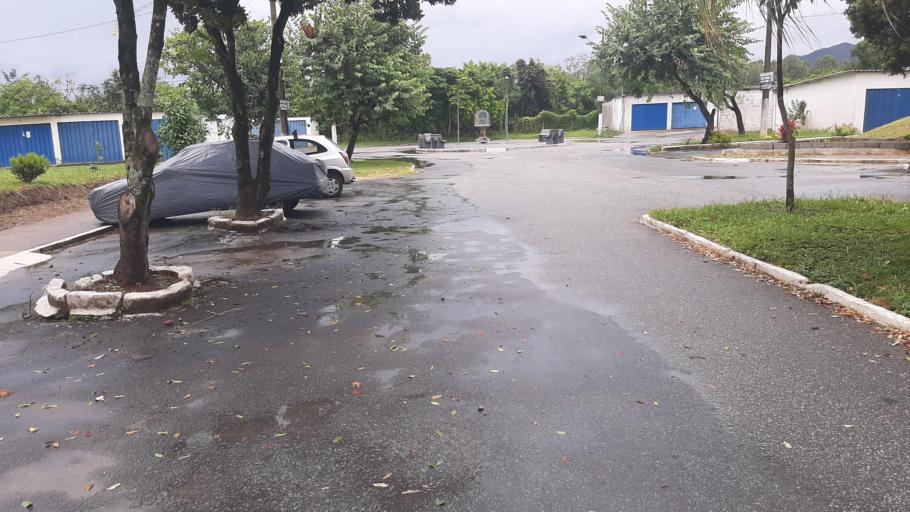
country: BR
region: Minas Gerais
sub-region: Sao Joao Del Rei
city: Sao Joao del Rei
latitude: -21.1255
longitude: -44.2353
